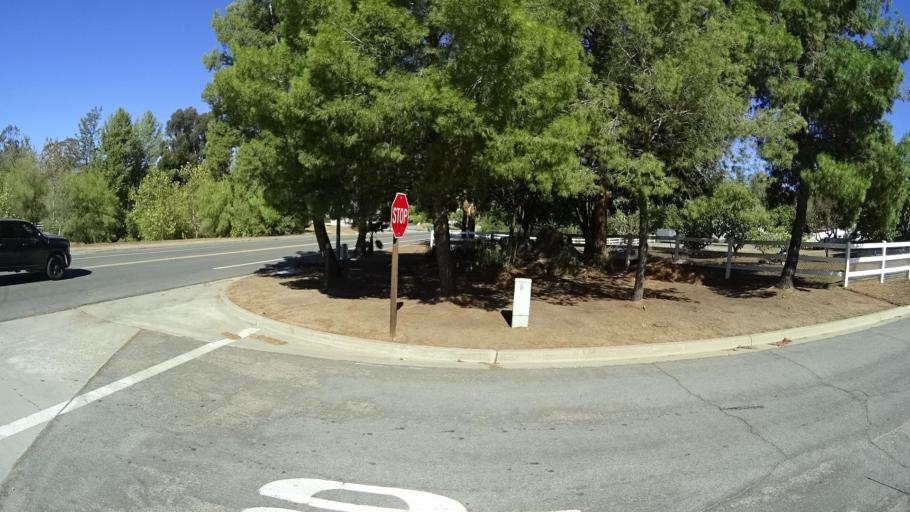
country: US
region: California
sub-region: San Diego County
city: Lakeside
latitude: 32.8633
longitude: -116.8731
